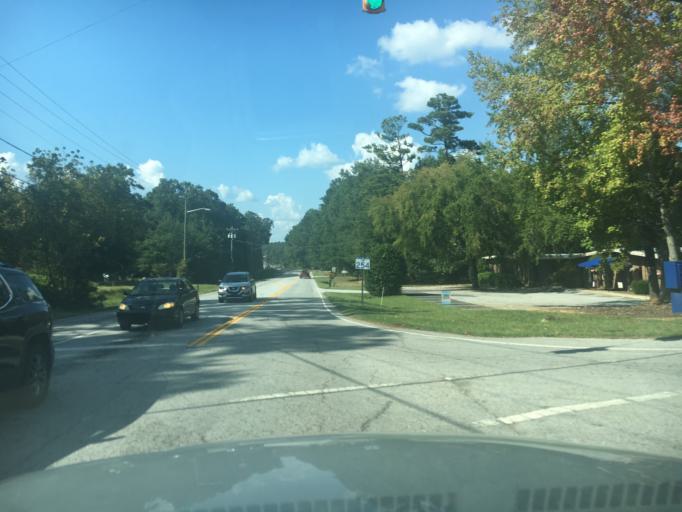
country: US
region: South Carolina
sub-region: Greenwood County
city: Greenwood
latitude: 34.2103
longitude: -82.1657
